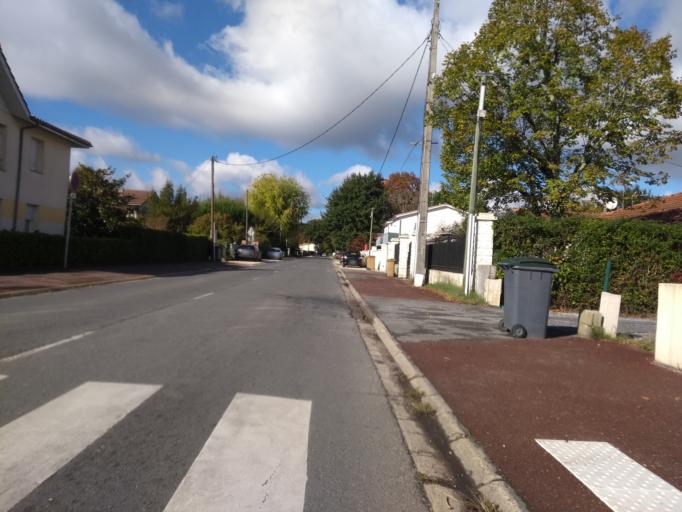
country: FR
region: Aquitaine
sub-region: Departement de la Gironde
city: Saint-Aubin-de-Medoc
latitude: 44.7729
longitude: -0.7027
